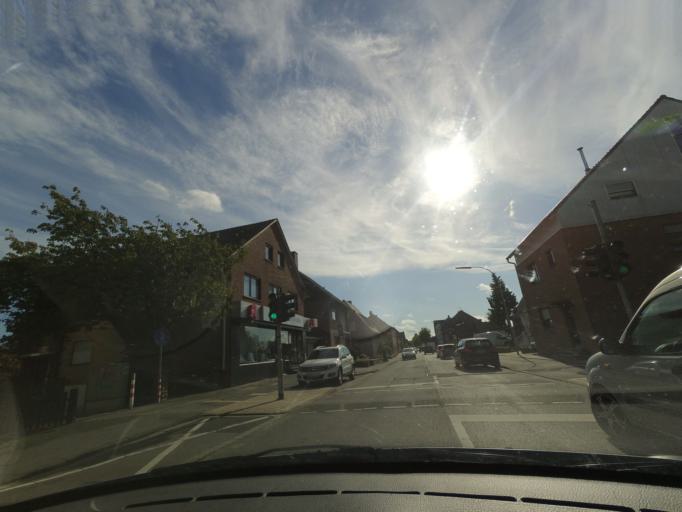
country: DE
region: North Rhine-Westphalia
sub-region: Regierungsbezirk Dusseldorf
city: Korschenbroich
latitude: 51.1946
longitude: 6.5540
